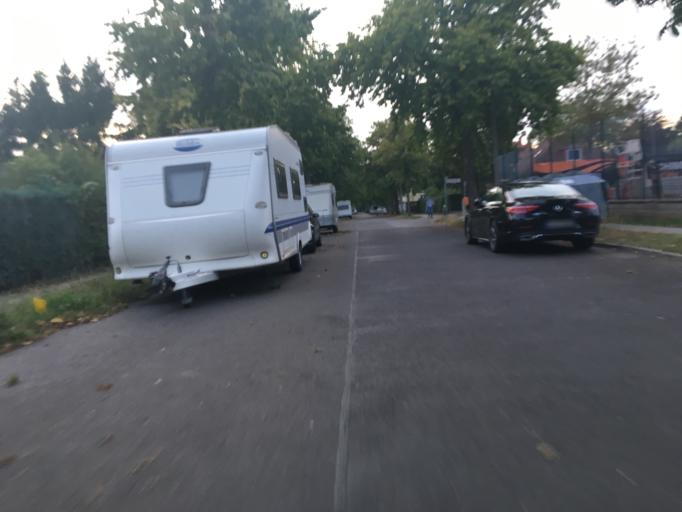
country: DE
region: Berlin
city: Alt-Hohenschoenhausen
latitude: 52.5445
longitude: 13.4855
